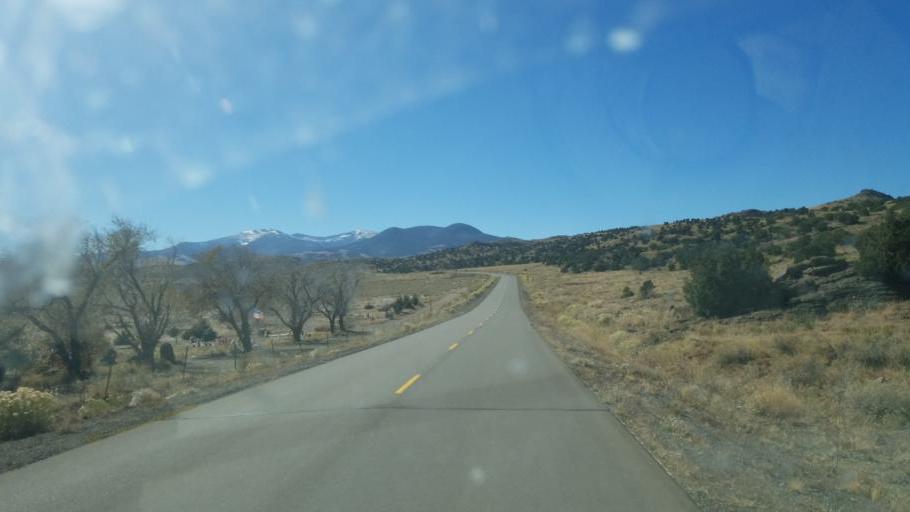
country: US
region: Colorado
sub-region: Rio Grande County
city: Del Norte
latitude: 37.6571
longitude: -106.3618
